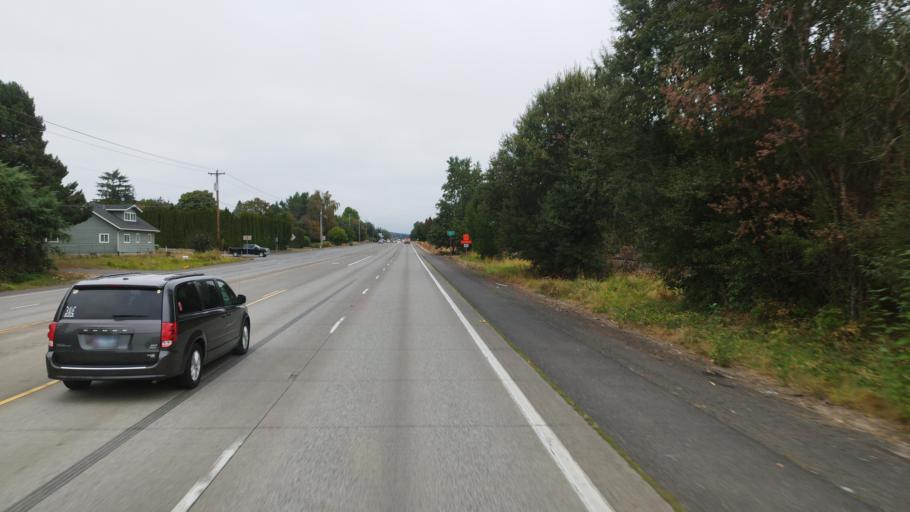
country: US
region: Oregon
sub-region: Columbia County
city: Warren
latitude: 45.8298
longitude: -122.8424
